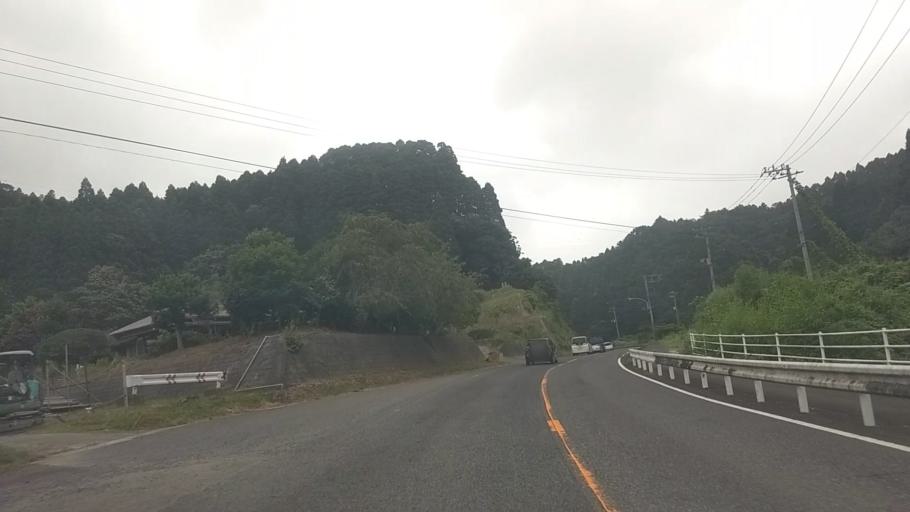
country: JP
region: Chiba
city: Ohara
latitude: 35.2656
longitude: 140.3636
